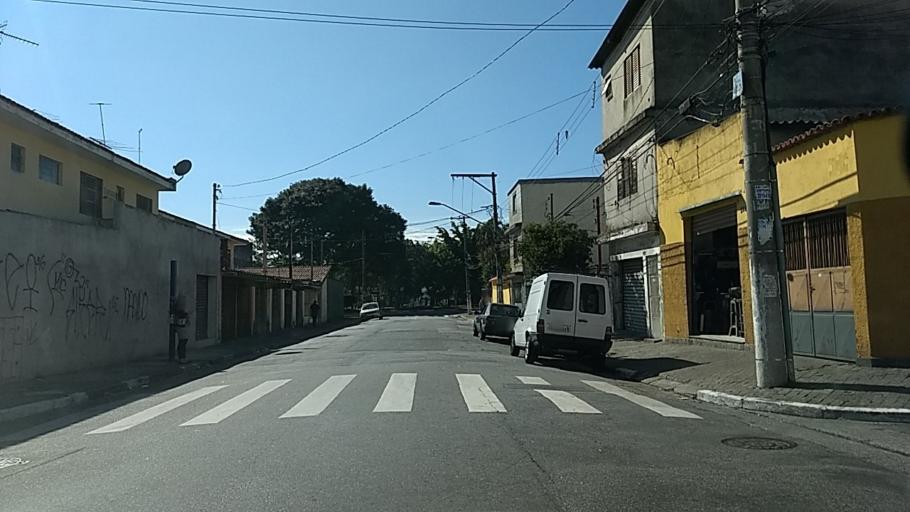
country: BR
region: Sao Paulo
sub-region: Guarulhos
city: Guarulhos
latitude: -23.4843
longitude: -46.5780
